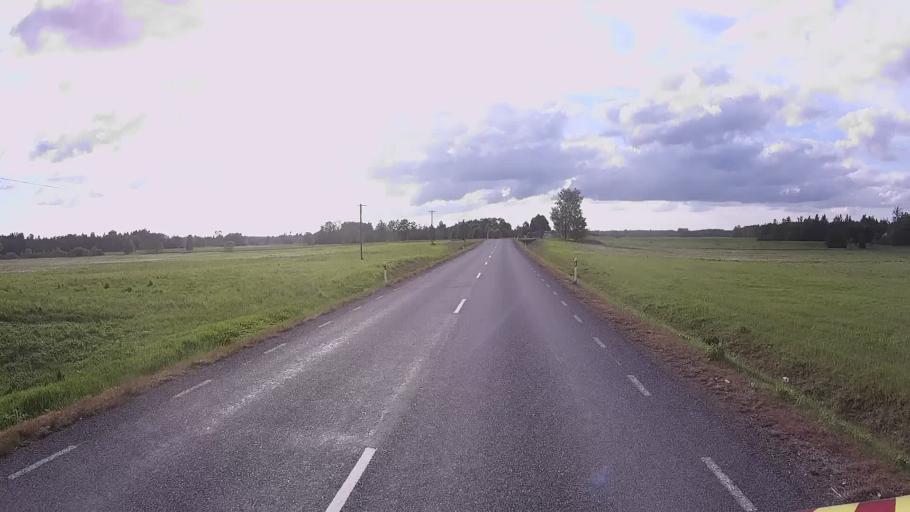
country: EE
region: Jogevamaa
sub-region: Mustvee linn
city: Mustvee
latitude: 59.0405
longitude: 27.0647
